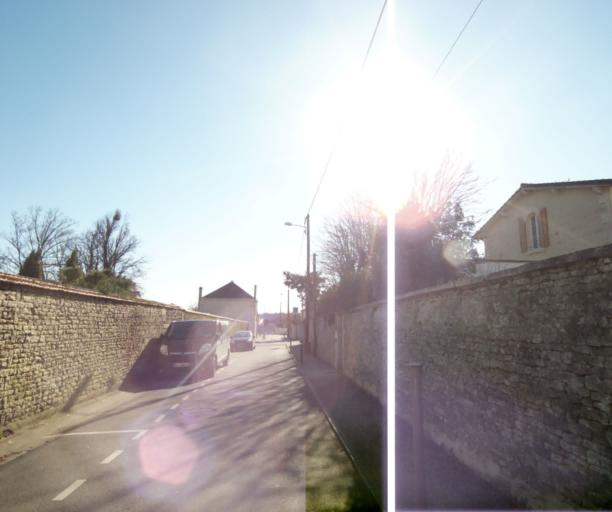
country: FR
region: Poitou-Charentes
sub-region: Departement des Deux-Sevres
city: Niort
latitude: 46.3459
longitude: -0.4723
